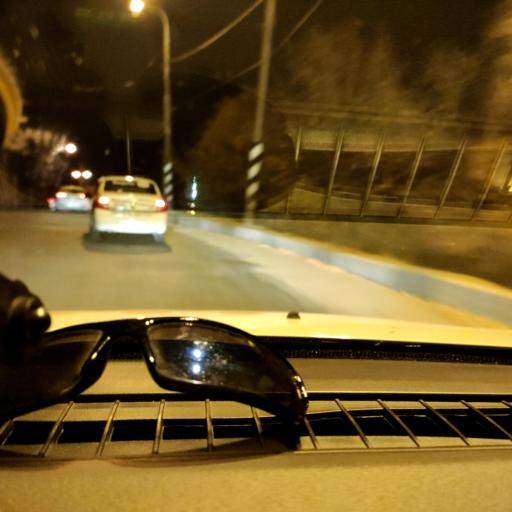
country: RU
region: Samara
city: Samara
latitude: 53.1513
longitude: 50.0925
